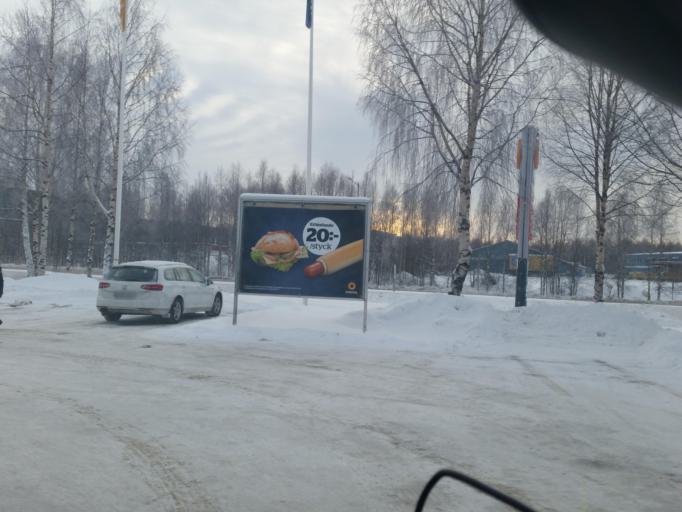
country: SE
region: Norrbotten
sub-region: Pitea Kommun
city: Pitea
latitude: 65.3105
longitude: 21.4980
